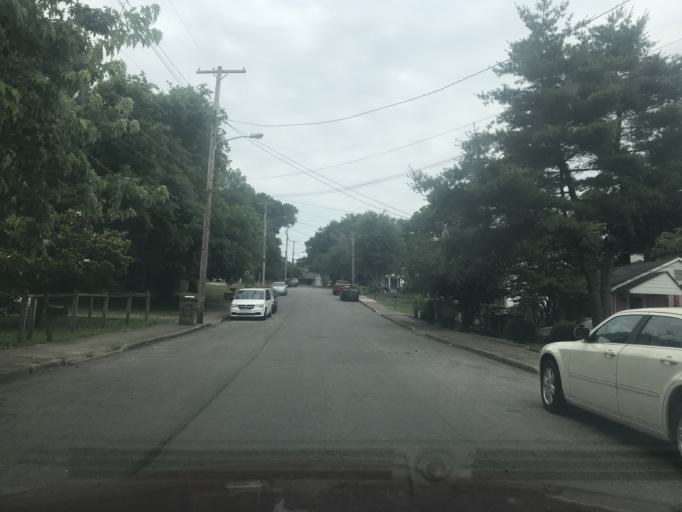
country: US
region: Tennessee
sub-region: Davidson County
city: Nashville
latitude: 36.1785
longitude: -86.8155
